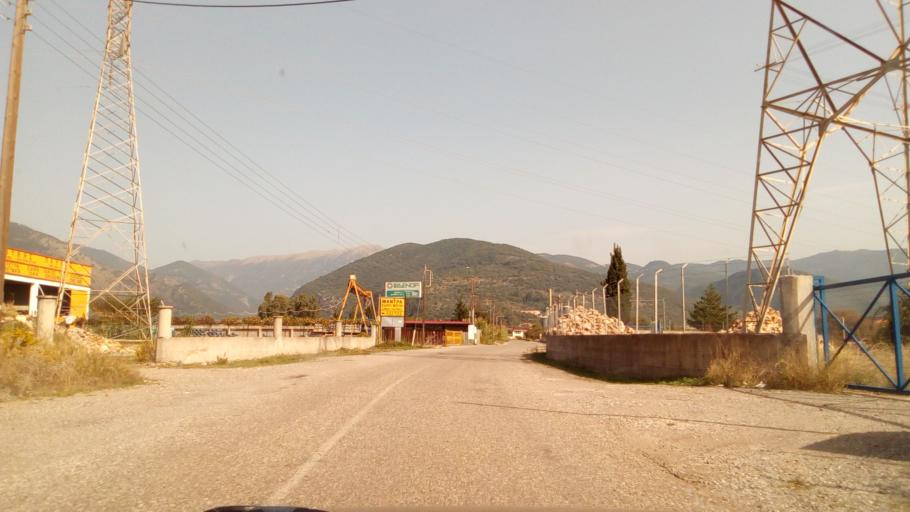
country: GR
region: West Greece
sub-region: Nomos Aitolias kai Akarnanias
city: Nafpaktos
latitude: 38.4097
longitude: 21.8809
